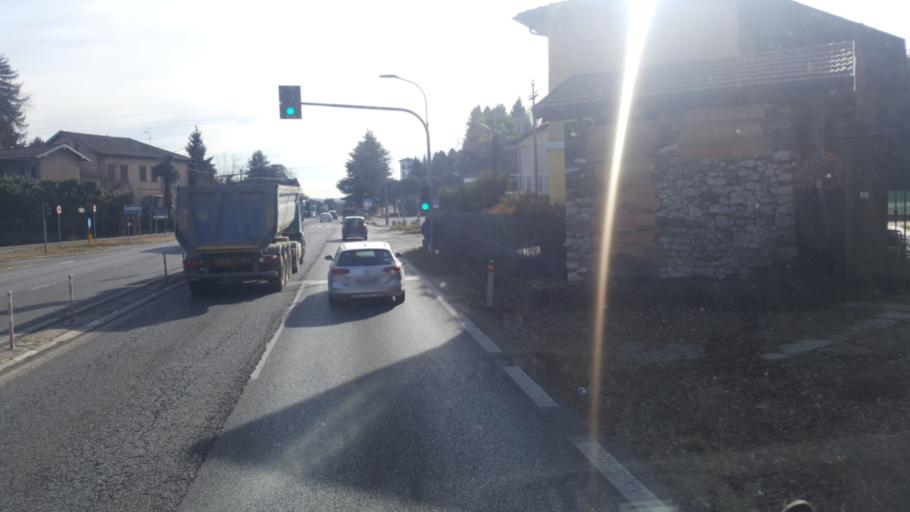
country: IT
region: Lombardy
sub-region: Provincia di Varese
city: Comabbio
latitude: 45.7732
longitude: 8.6791
